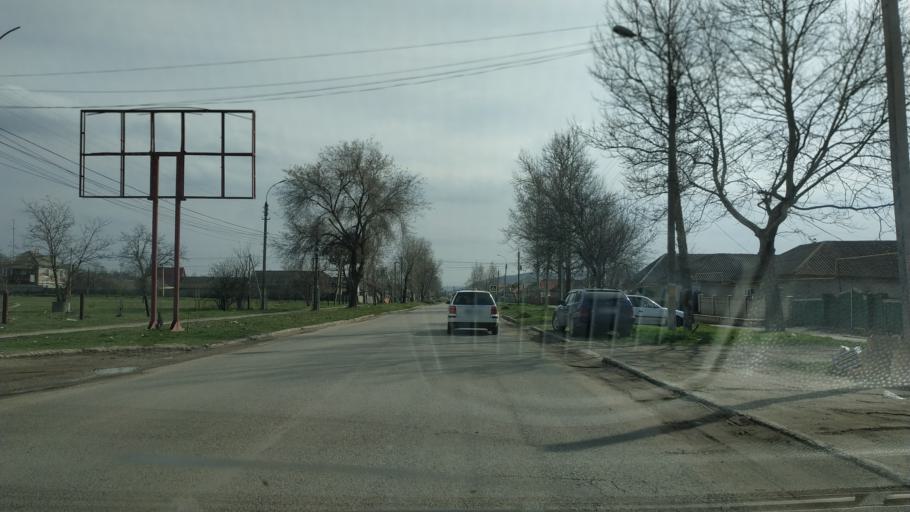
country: MD
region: Gagauzia
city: Vulcanesti
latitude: 45.6812
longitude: 28.4083
